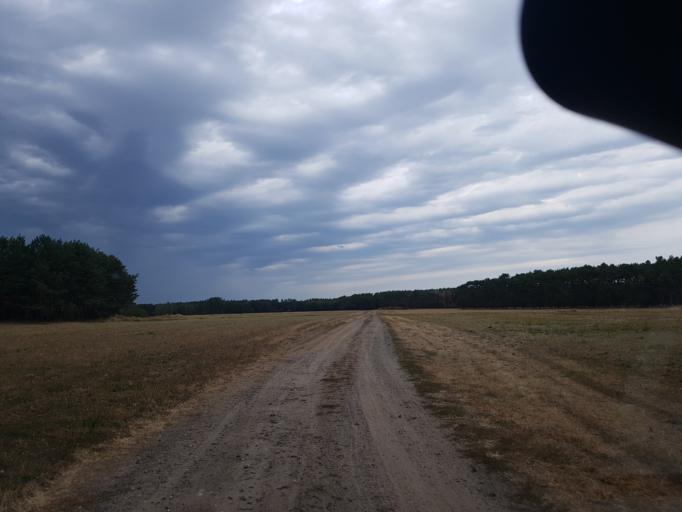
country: DE
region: Brandenburg
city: Schilda
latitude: 51.5573
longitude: 13.3268
